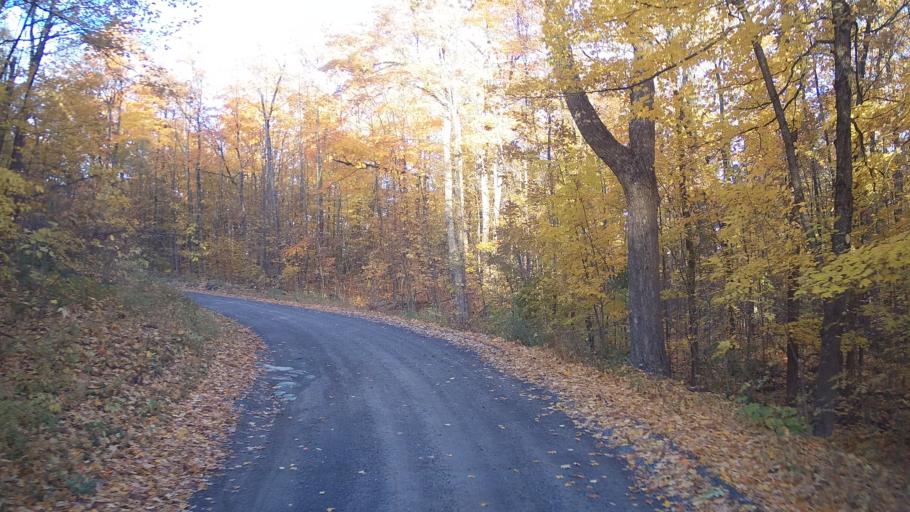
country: CA
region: Ontario
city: Arnprior
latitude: 45.3406
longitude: -76.3496
